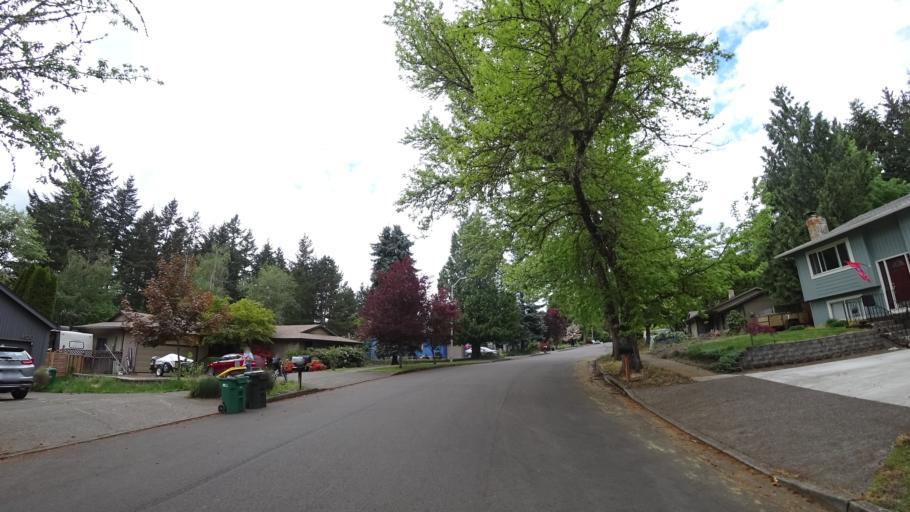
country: US
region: Oregon
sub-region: Washington County
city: Beaverton
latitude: 45.4724
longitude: -122.8301
